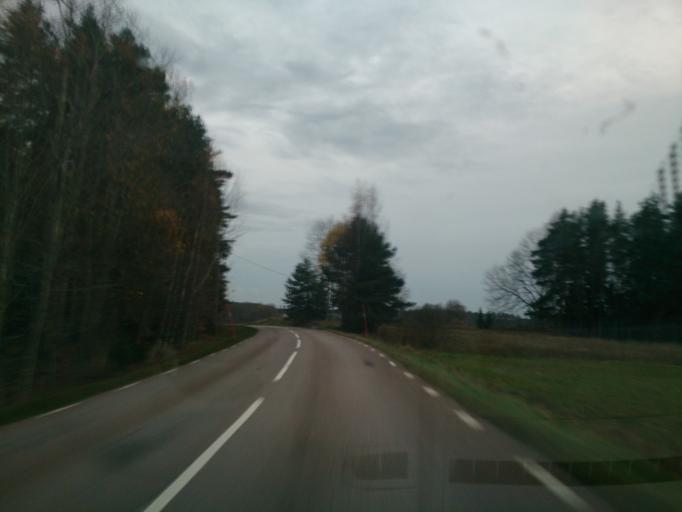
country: SE
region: OEstergoetland
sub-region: Linkopings Kommun
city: Linghem
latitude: 58.4566
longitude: 15.8844
